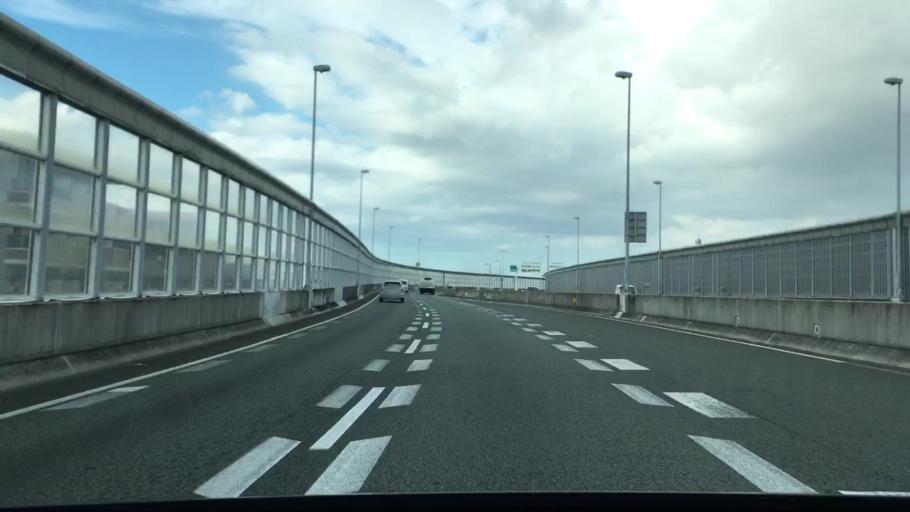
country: JP
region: Fukuoka
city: Fukuoka-shi
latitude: 33.5853
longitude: 130.3406
